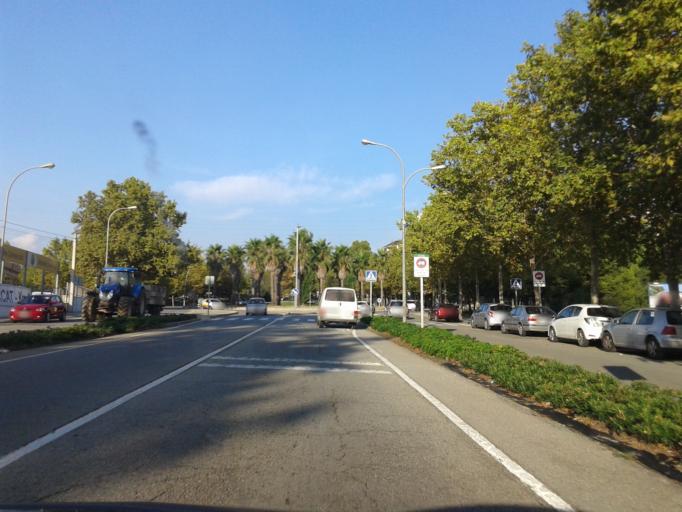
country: ES
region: Catalonia
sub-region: Provincia de Barcelona
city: Vilafranca del Penedes
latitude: 41.3384
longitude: 1.6899
